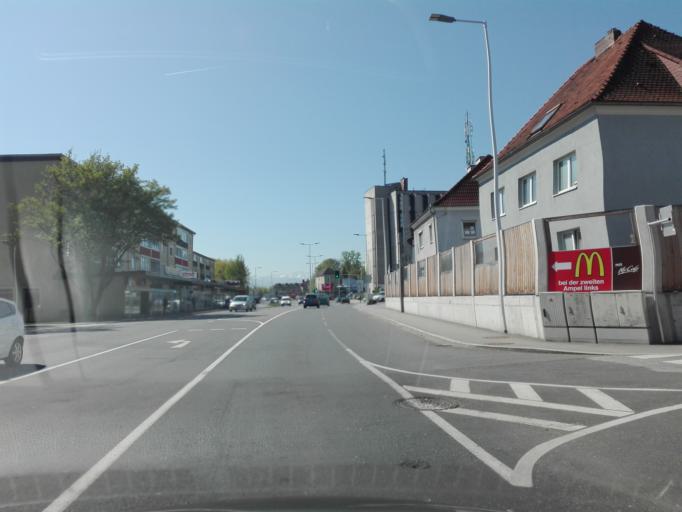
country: AT
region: Upper Austria
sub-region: Steyr Stadt
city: Steyr
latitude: 48.0522
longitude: 14.4204
